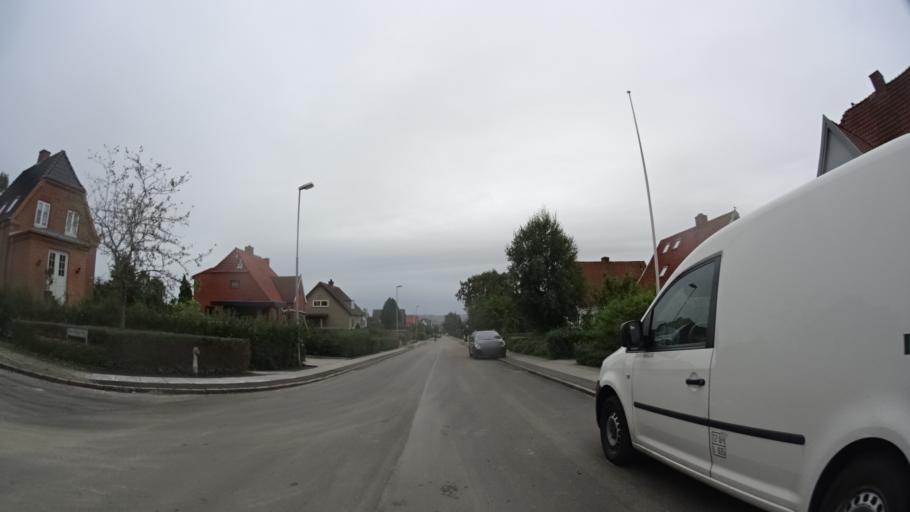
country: DK
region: Central Jutland
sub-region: Arhus Kommune
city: Stavtrup
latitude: 56.1561
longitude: 10.1475
